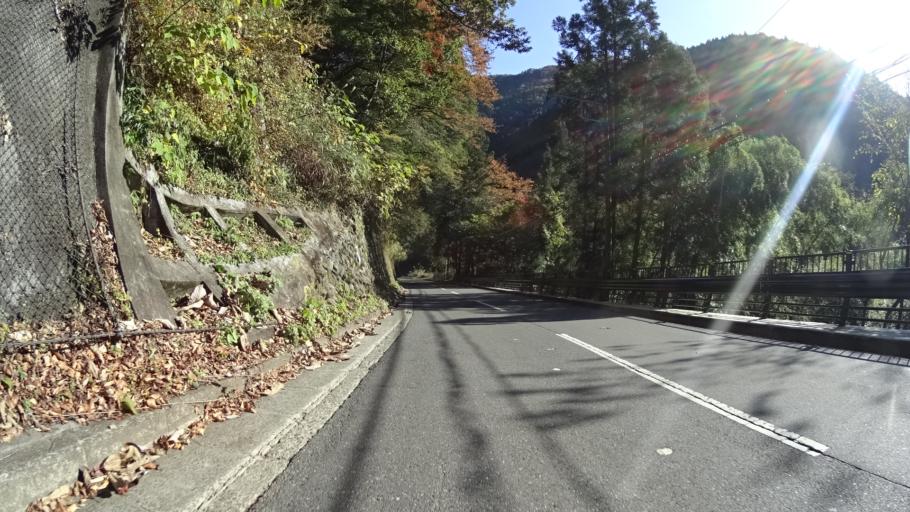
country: JP
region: Yamanashi
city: Uenohara
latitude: 35.7024
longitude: 139.1088
